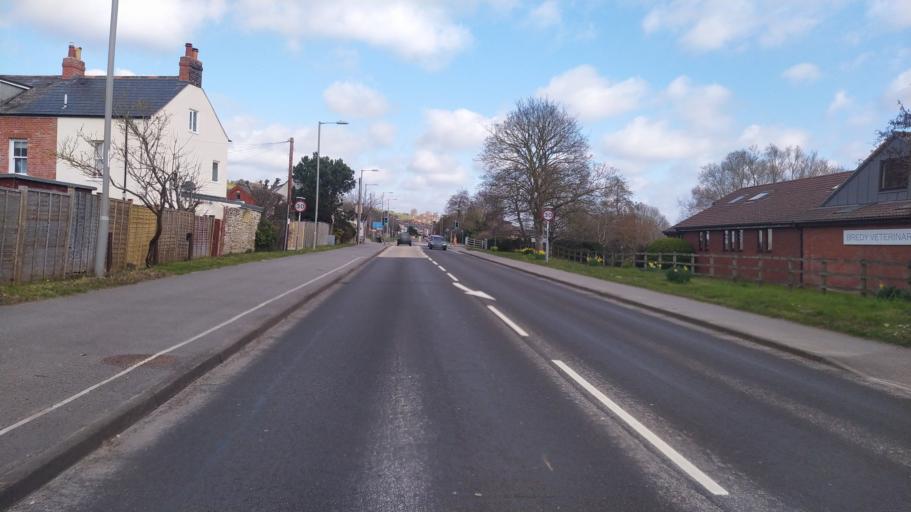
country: GB
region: England
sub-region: Dorset
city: Bridport
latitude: 50.7364
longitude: -2.7479
